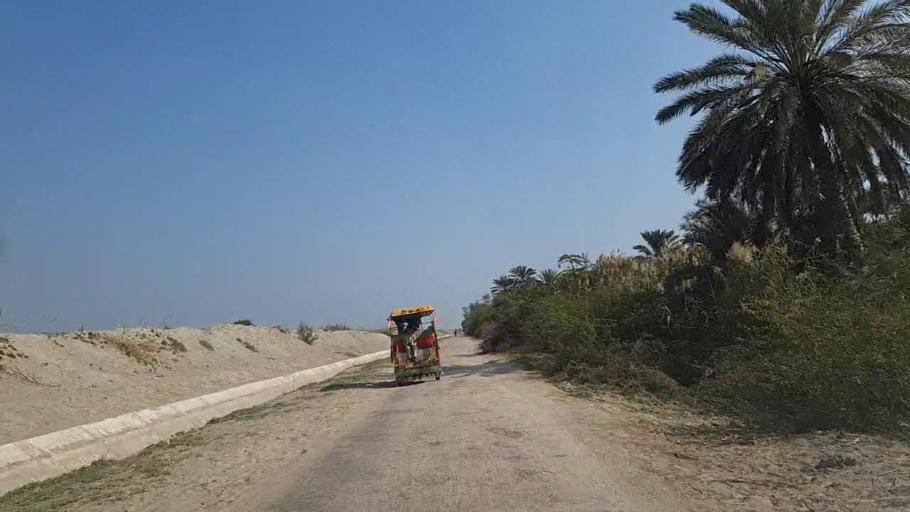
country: PK
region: Sindh
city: Jam Sahib
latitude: 26.2718
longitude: 68.5602
